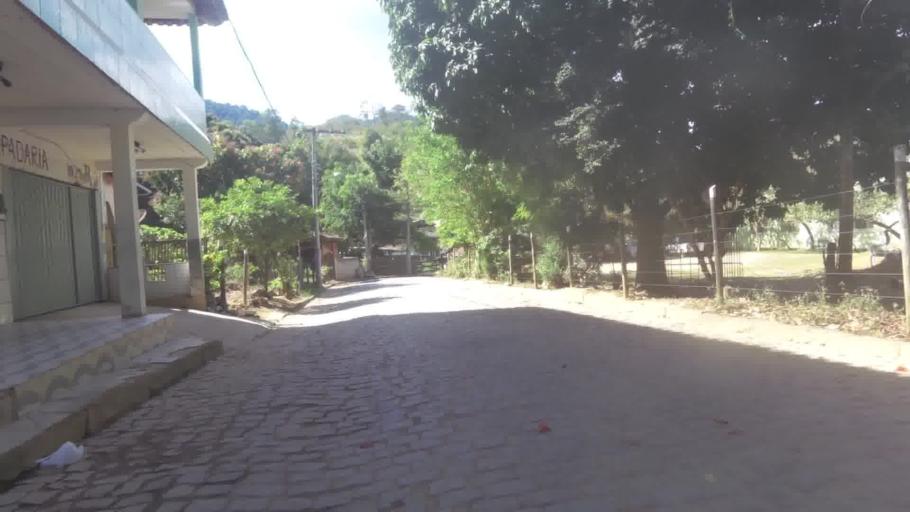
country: BR
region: Espirito Santo
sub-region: Vargem Alta
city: Vargem Alta
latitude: -20.6620
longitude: -41.0579
